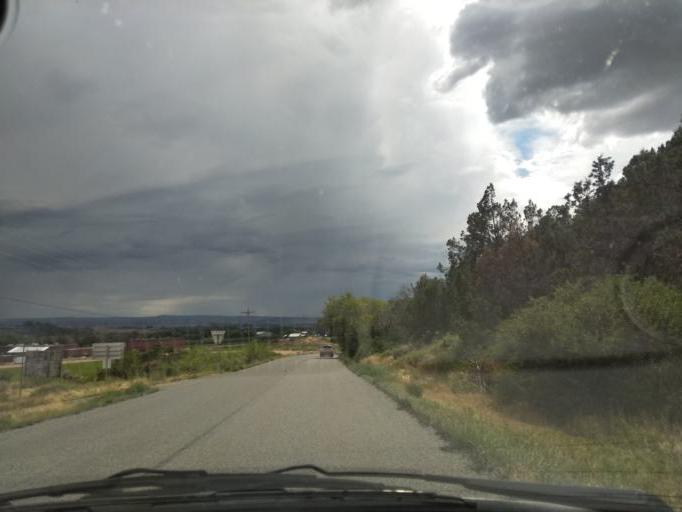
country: US
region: Colorado
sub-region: Delta County
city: Paonia
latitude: 38.8799
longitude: -107.5984
